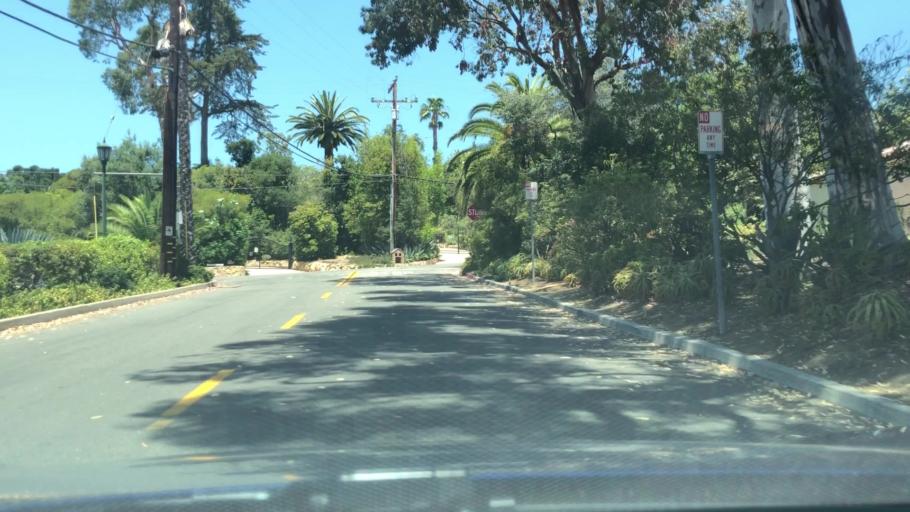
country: US
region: California
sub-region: Santa Barbara County
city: Mission Canyon
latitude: 34.4395
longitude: -119.7047
